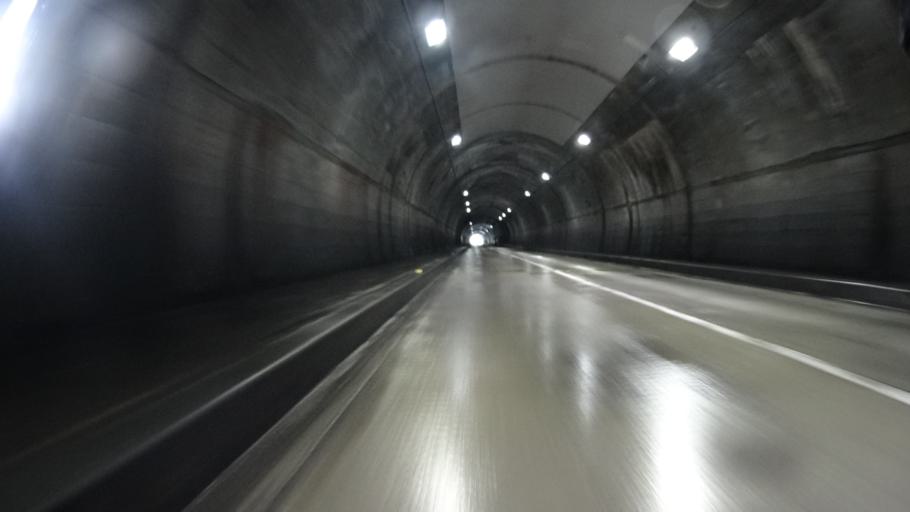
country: JP
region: Tokyo
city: Ome
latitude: 35.8344
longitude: 139.2090
